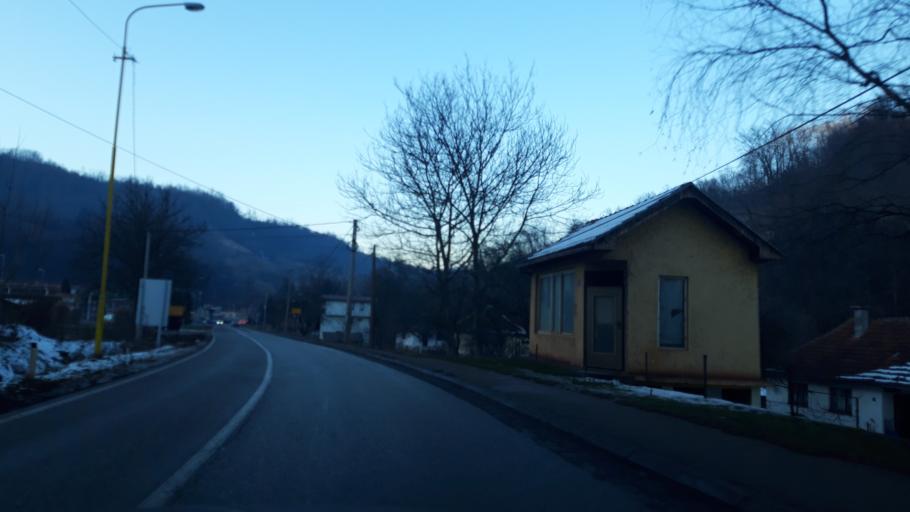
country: BA
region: Republika Srpska
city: Milici
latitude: 44.1735
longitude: 19.0767
